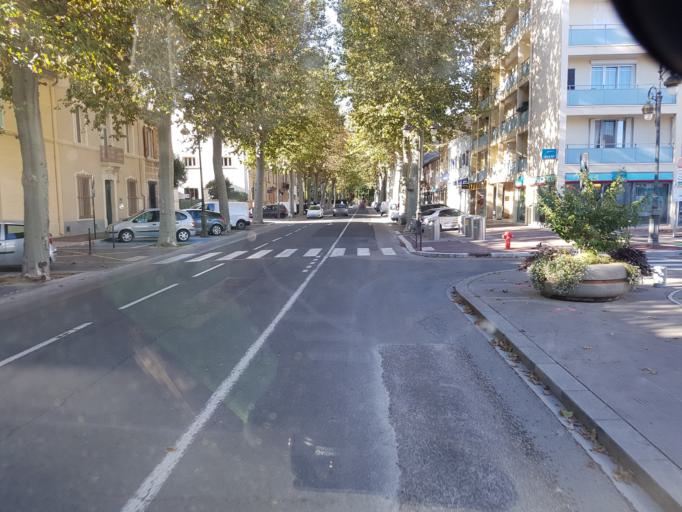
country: FR
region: Languedoc-Roussillon
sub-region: Departement de l'Aude
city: Narbonne
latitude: 43.1854
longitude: 3.0096
